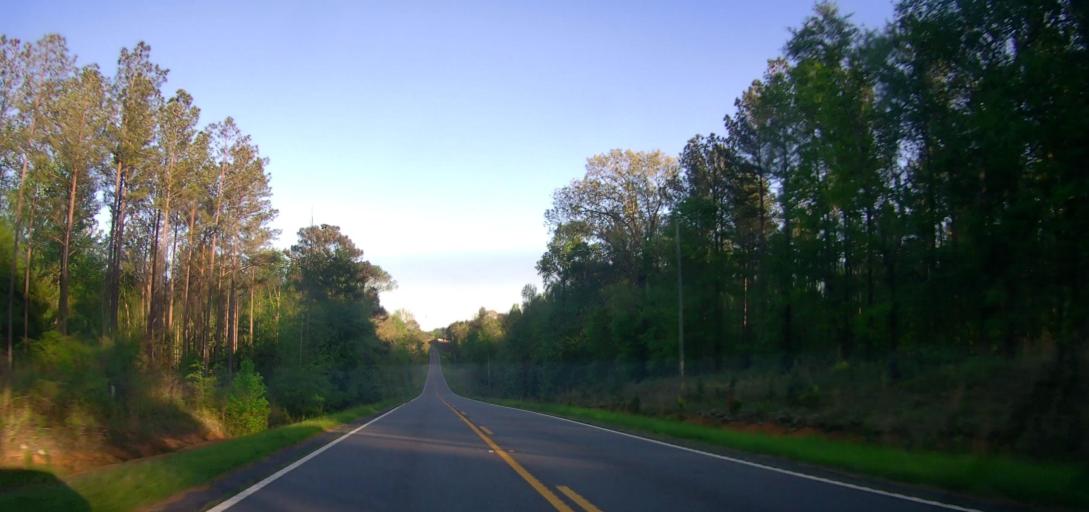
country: US
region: Georgia
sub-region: Schley County
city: Ellaville
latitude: 32.3498
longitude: -84.3775
